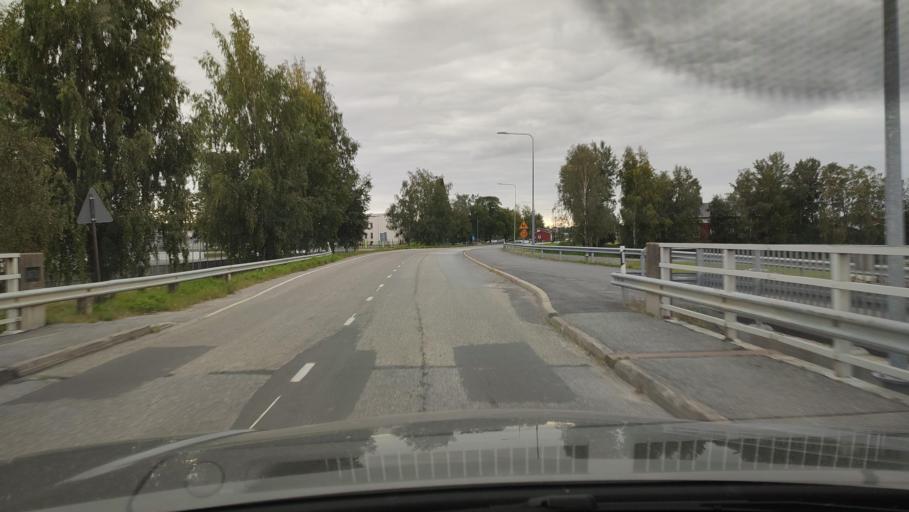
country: FI
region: Ostrobothnia
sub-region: Sydosterbotten
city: Kristinestad
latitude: 62.2559
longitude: 21.5263
